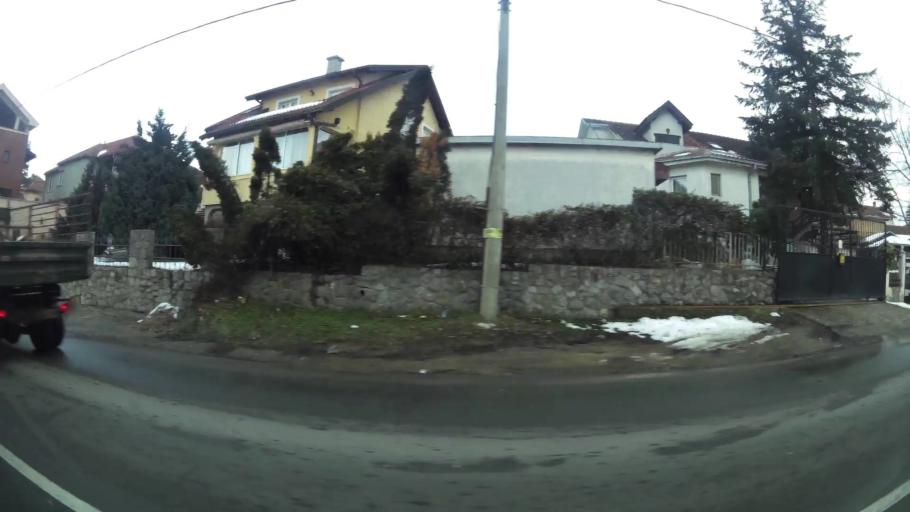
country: RS
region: Central Serbia
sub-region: Belgrade
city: Vozdovac
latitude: 44.7371
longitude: 20.4855
